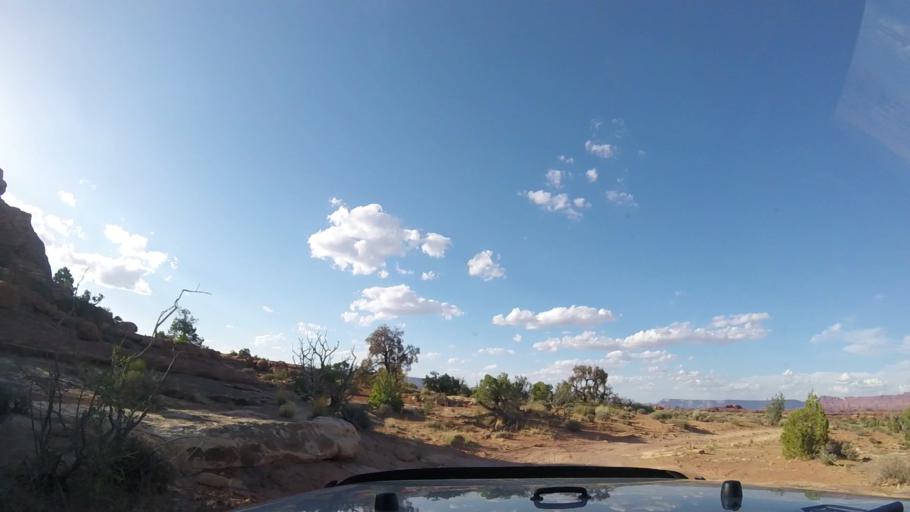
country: US
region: Utah
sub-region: Grand County
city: Moab
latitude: 38.2125
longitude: -109.8062
